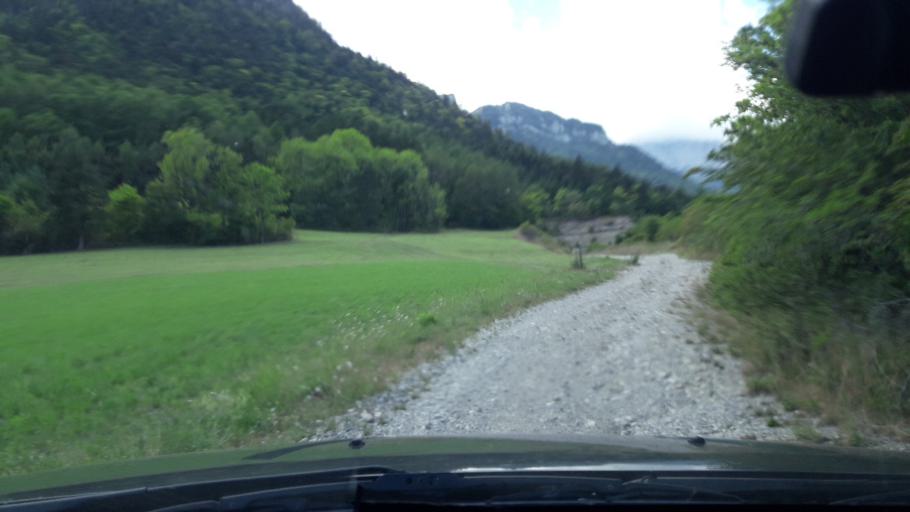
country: FR
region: Rhone-Alpes
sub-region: Departement de l'Isere
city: La Motte-Saint-Martin
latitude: 44.8613
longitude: 5.5994
